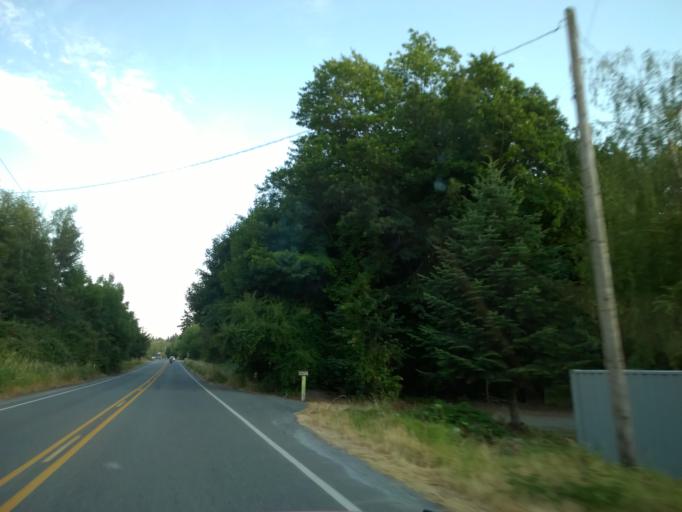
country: US
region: Washington
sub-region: King County
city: Woodinville
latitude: 47.7209
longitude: -122.1350
